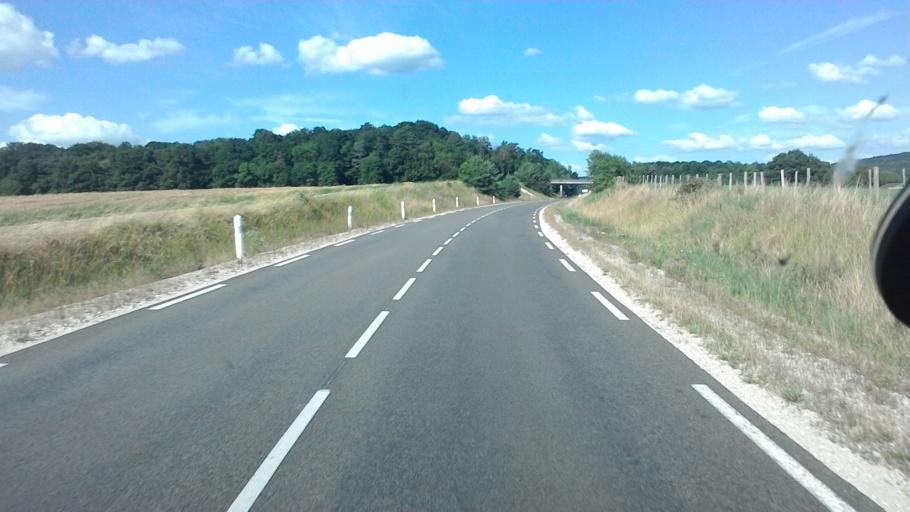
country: FR
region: Franche-Comte
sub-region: Departement de la Haute-Saone
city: Rioz
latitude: 47.5110
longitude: 5.9889
